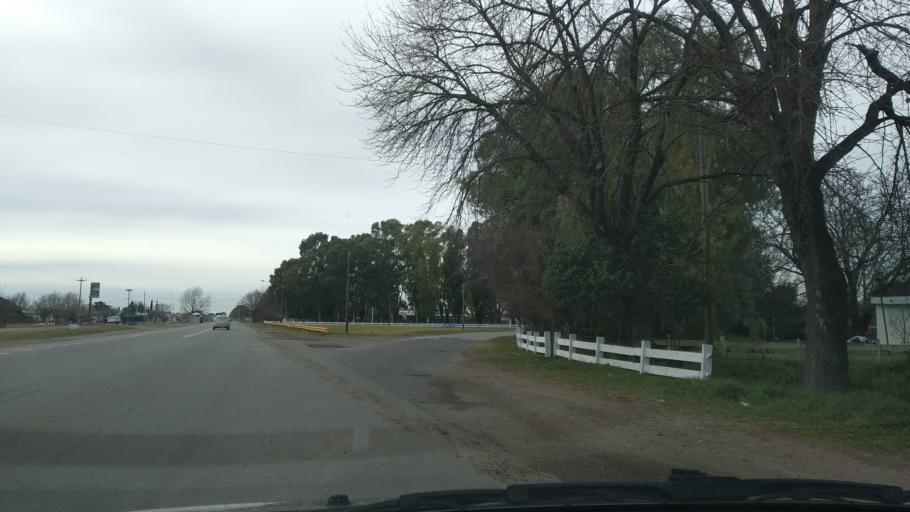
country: AR
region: Buenos Aires
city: Olavarria
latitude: -36.9828
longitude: -60.2885
